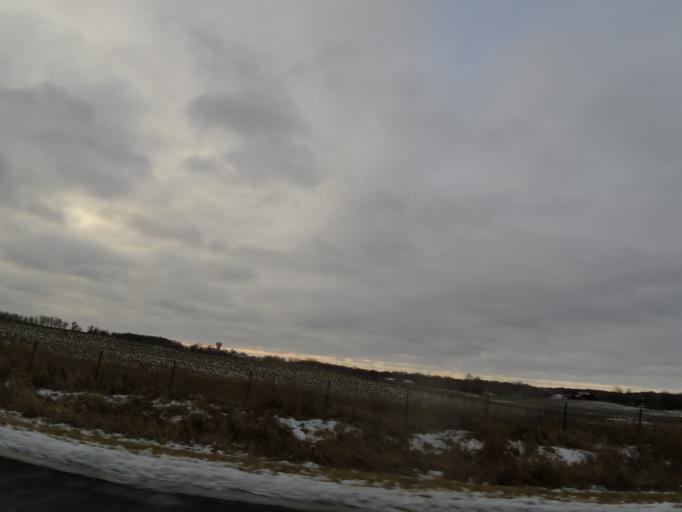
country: US
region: Minnesota
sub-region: Carver County
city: Carver
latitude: 44.7872
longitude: -93.6321
